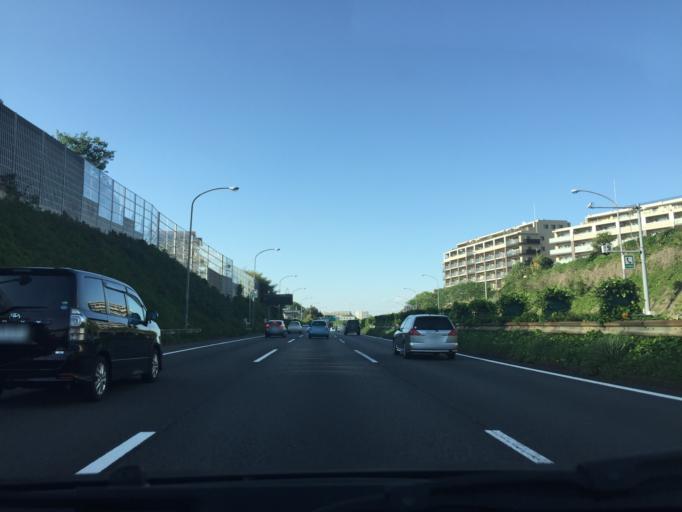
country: JP
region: Tokyo
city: Chofugaoka
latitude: 35.5813
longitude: 139.5651
